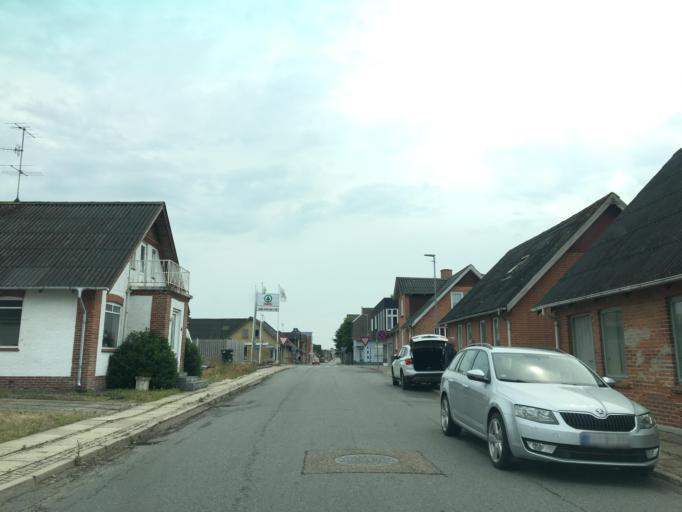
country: DK
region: North Denmark
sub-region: Thisted Kommune
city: Hurup
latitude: 56.8089
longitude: 8.4043
